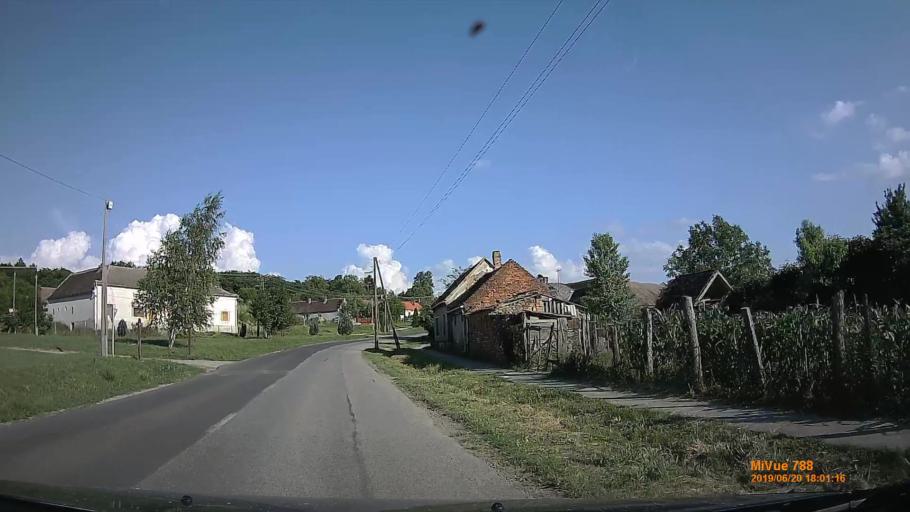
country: HU
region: Baranya
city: Buekkoesd
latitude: 46.0841
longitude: 17.9889
